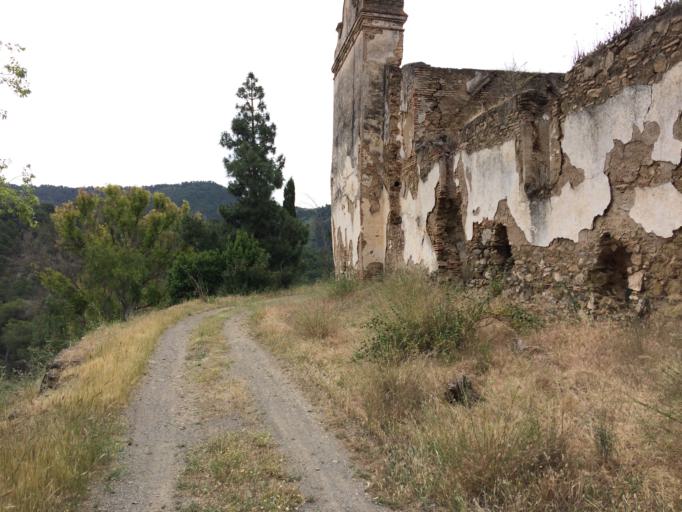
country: ES
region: Andalusia
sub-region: Provincia de Malaga
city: Casabermeja
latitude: 36.8277
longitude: -4.4160
